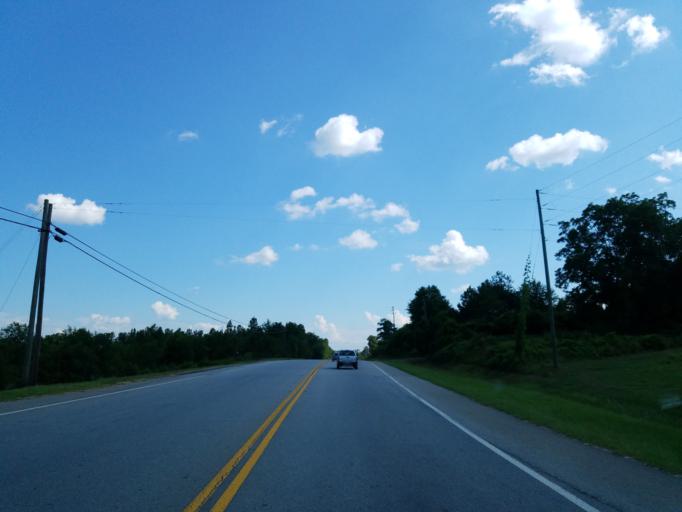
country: US
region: Georgia
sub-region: Crawford County
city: Roberta
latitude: 32.7329
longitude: -84.0162
